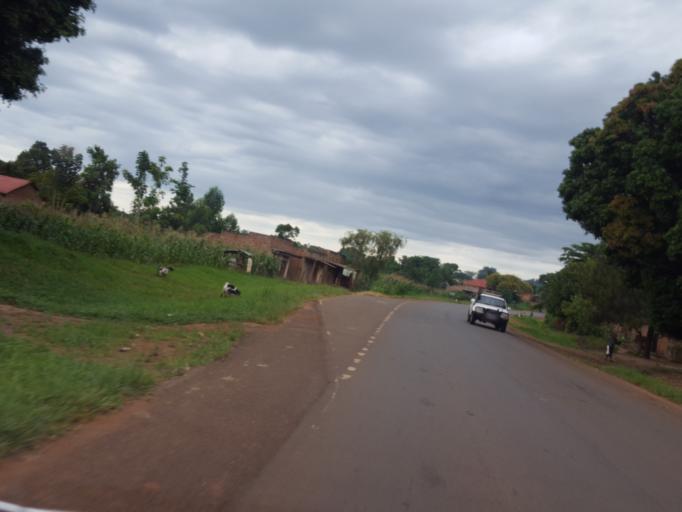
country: UG
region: Central Region
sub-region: Kiboga District
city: Kiboga
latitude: 0.8692
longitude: 31.8557
